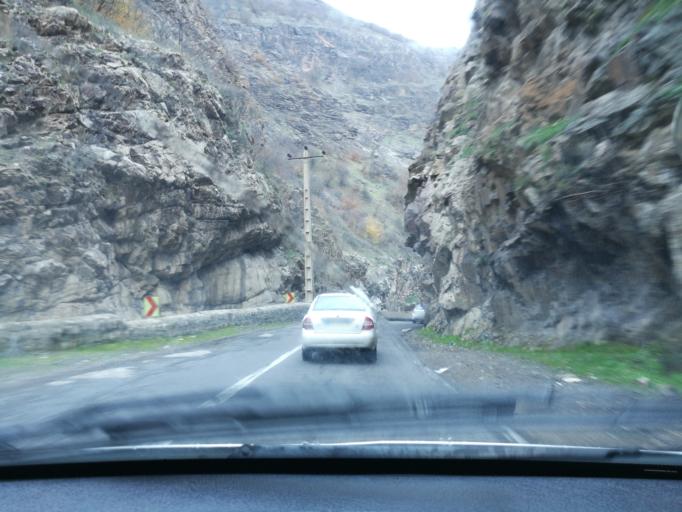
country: IR
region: Mazandaran
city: Chalus
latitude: 36.2910
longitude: 51.2394
